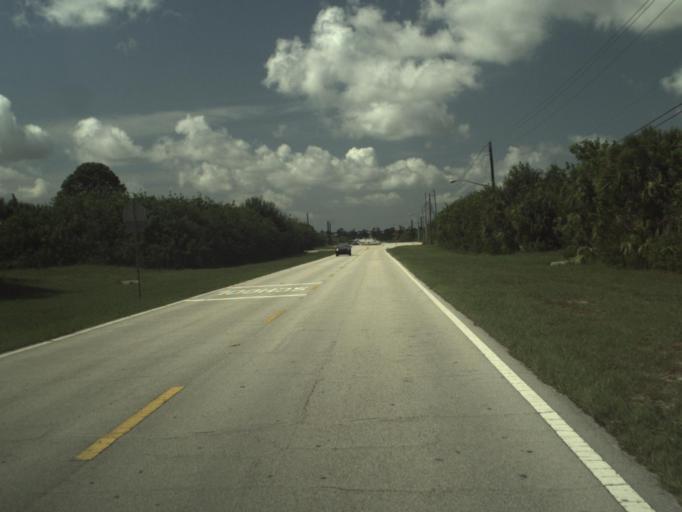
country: US
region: Florida
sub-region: Saint Lucie County
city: Port Saint Lucie
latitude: 27.2141
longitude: -80.3720
